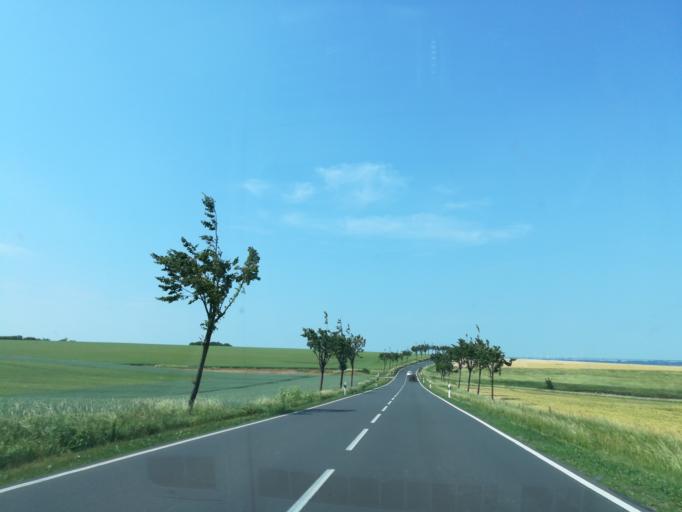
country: DE
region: Saxony-Anhalt
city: Schneidlingen
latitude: 51.8701
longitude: 11.4479
